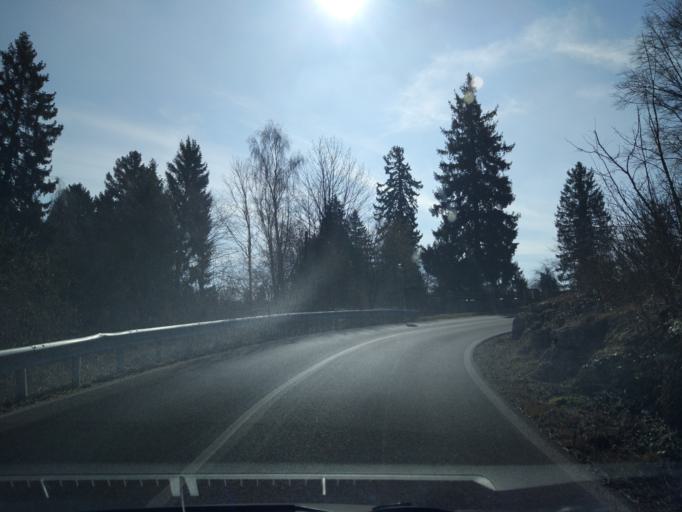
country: IT
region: Veneto
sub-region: Provincia di Verona
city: Erbezzo
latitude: 45.6456
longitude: 11.0027
